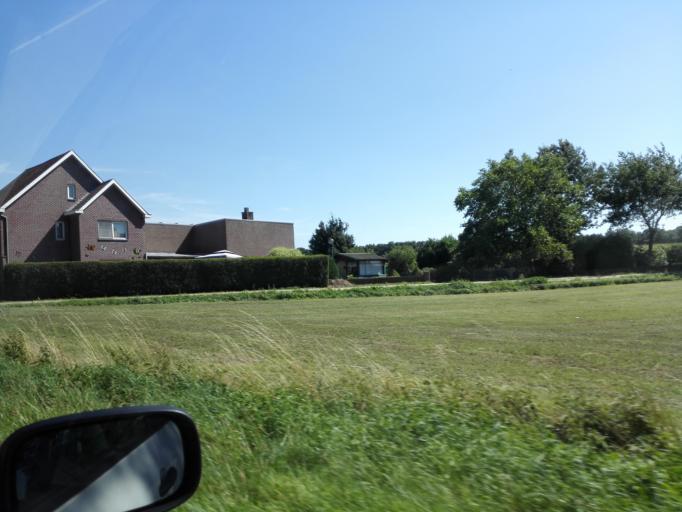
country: BE
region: Flanders
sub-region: Provincie Limburg
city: Bree
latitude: 51.0933
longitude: 5.5999
